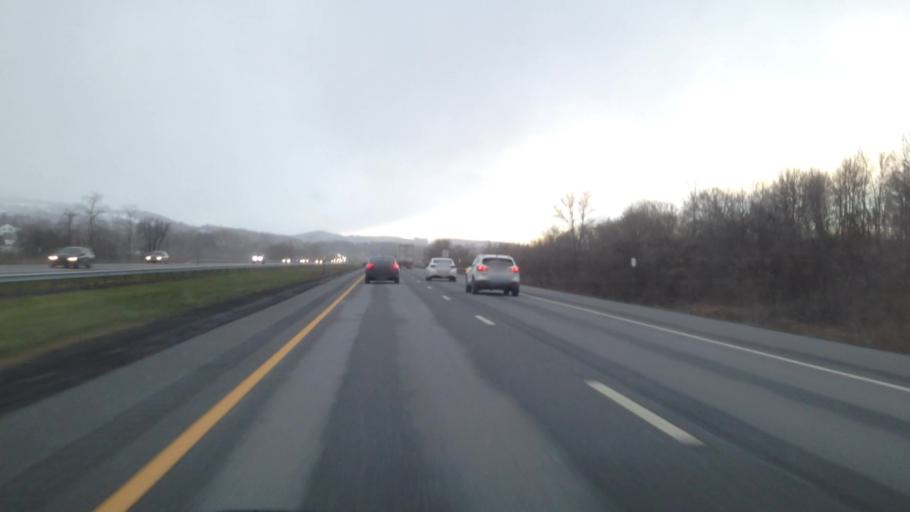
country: US
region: New York
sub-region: Montgomery County
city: Saint Johnsville
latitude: 43.0023
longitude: -74.7614
